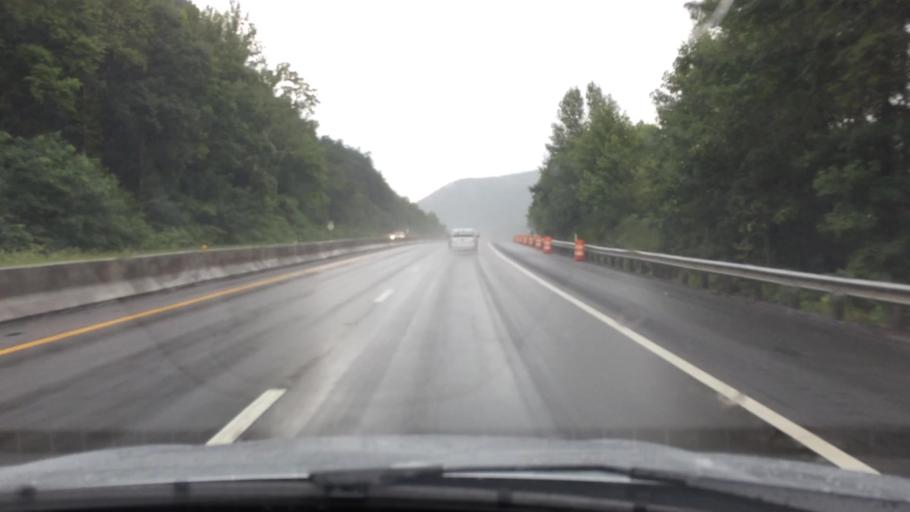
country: US
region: Tennessee
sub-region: Cocke County
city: Newport
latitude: 35.8309
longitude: -83.1828
